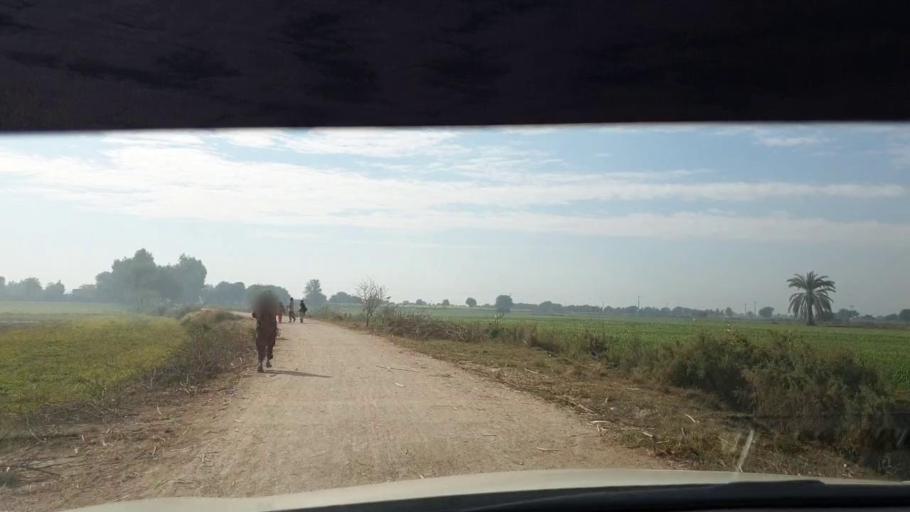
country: PK
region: Sindh
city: Berani
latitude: 25.7296
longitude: 68.8659
